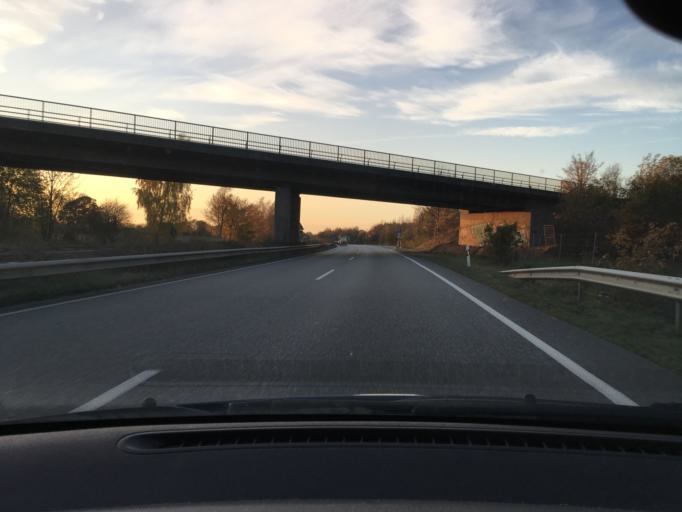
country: DE
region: Schleswig-Holstein
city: Bebensee
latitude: 53.8894
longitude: 10.2986
